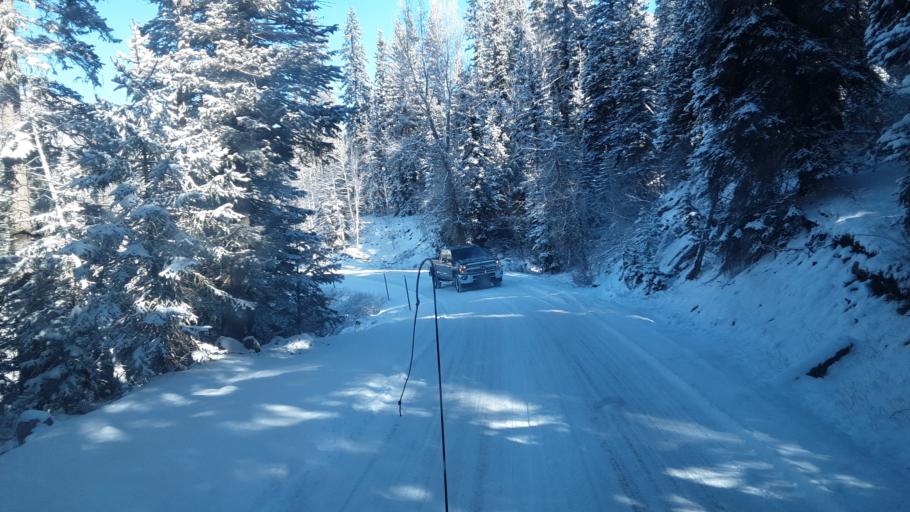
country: US
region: Colorado
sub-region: La Plata County
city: Bayfield
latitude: 37.4425
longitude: -107.6793
